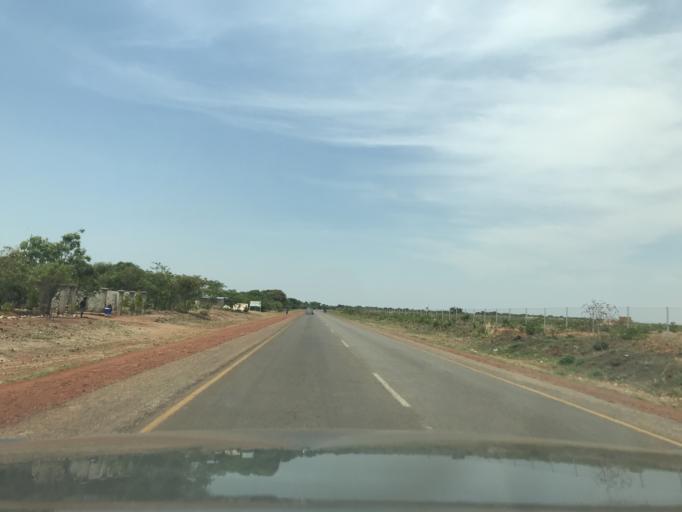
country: ZM
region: Northern
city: Kasama
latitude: -10.2192
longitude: 31.1395
